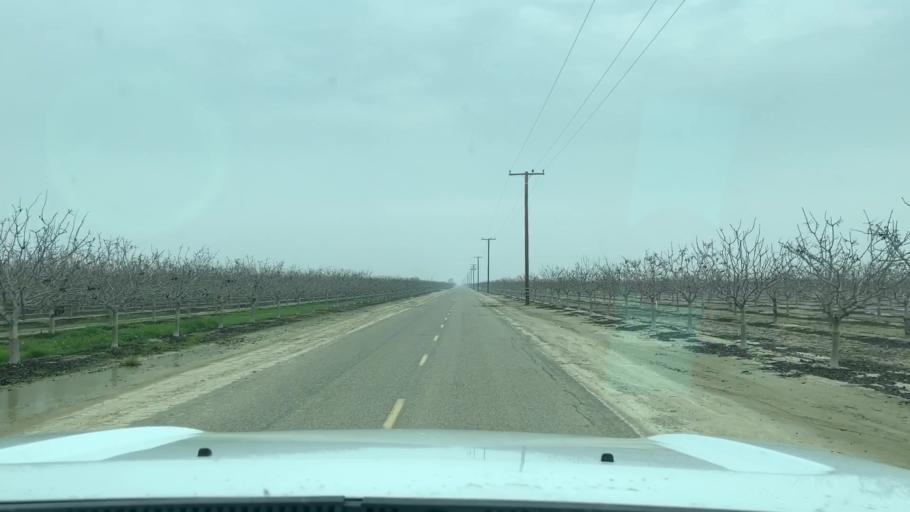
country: US
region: California
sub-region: Tulare County
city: Earlimart
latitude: 35.8193
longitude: -119.3481
